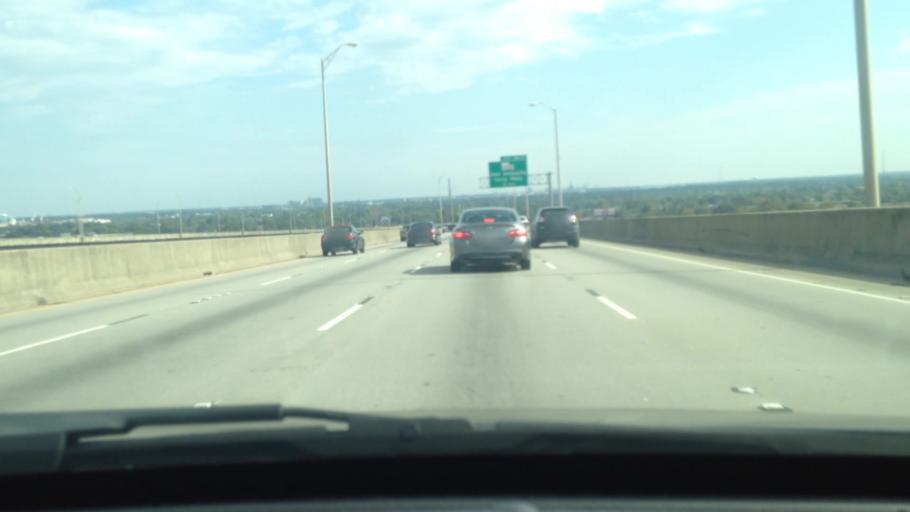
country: US
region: Louisiana
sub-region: Jefferson Parish
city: Gretna
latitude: 29.9378
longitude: -90.0519
